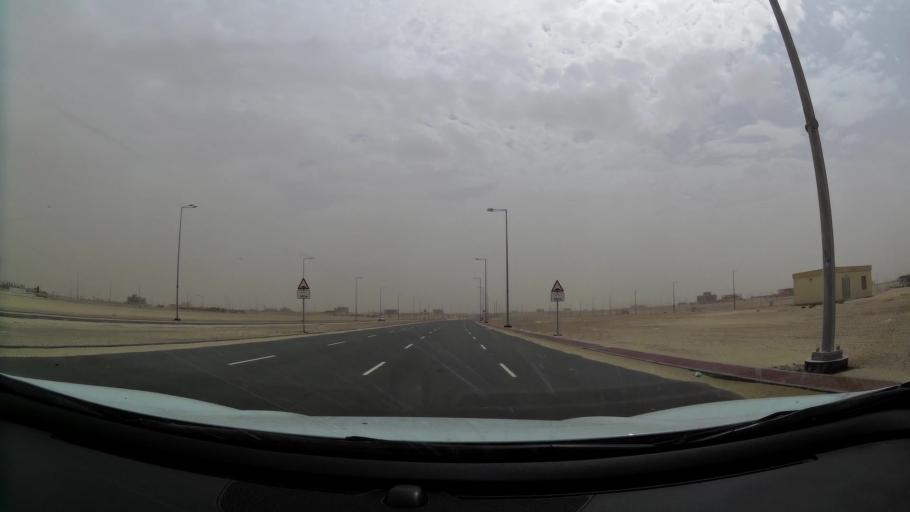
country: AE
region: Abu Dhabi
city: Abu Dhabi
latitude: 24.3690
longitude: 54.7495
